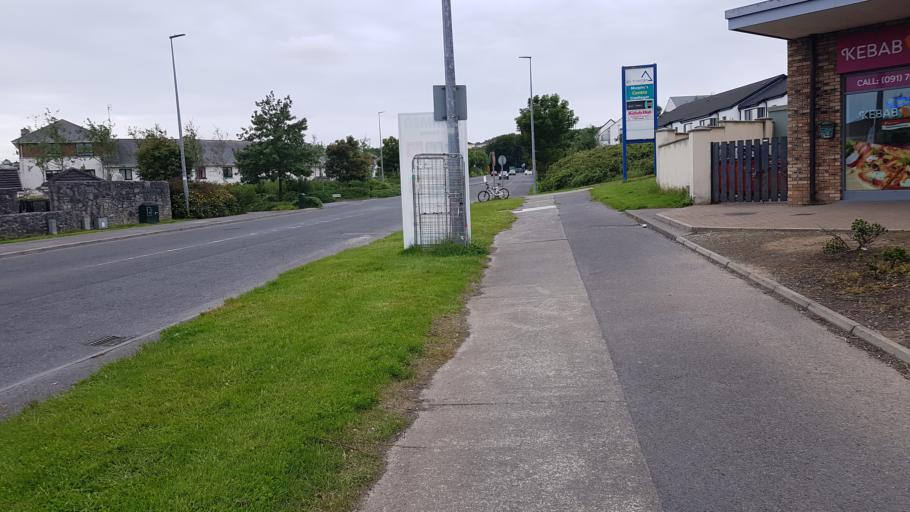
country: IE
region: Connaught
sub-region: County Galway
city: Gaillimh
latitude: 53.2964
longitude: -9.0311
